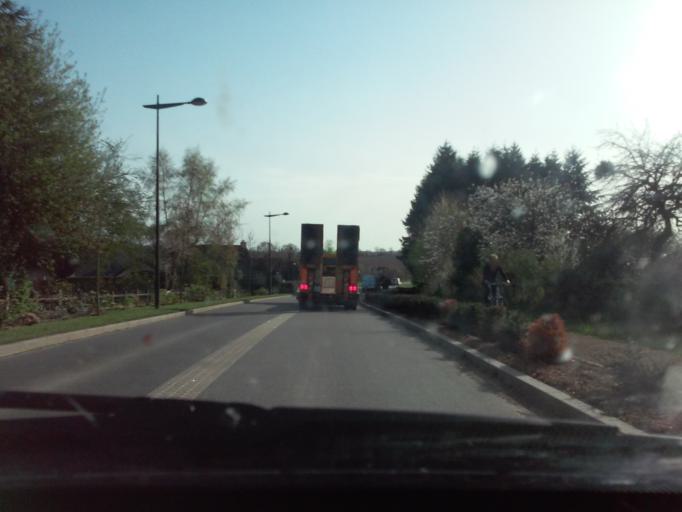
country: FR
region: Brittany
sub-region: Departement d'Ille-et-Vilaine
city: Saint-Jean-sur-Couesnon
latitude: 48.2885
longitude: -1.3712
